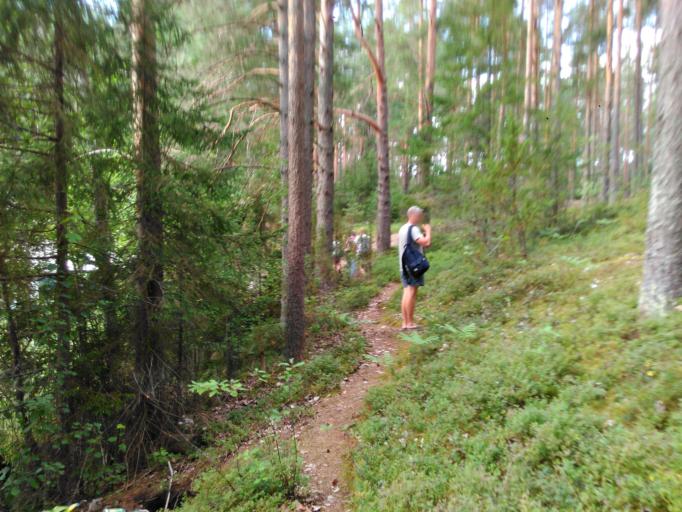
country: RU
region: Tverskaya
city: Ostashkov
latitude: 57.2389
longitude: 33.0161
